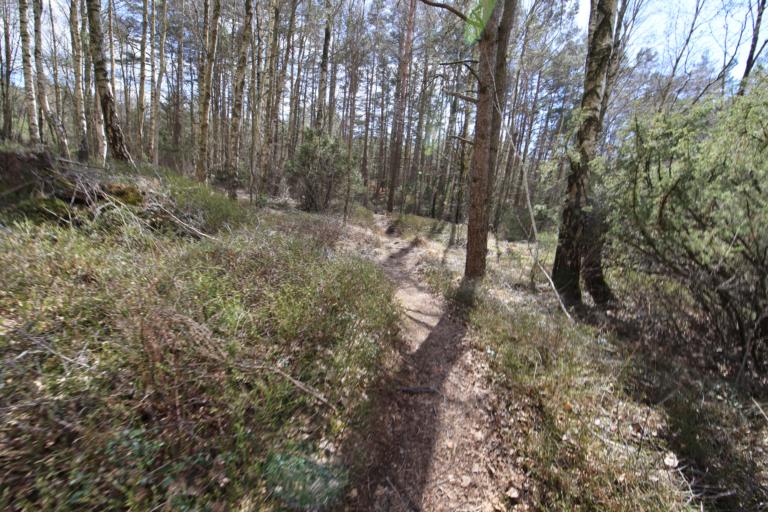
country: SE
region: Halland
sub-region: Varbergs Kommun
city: Varberg
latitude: 57.1789
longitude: 12.2384
